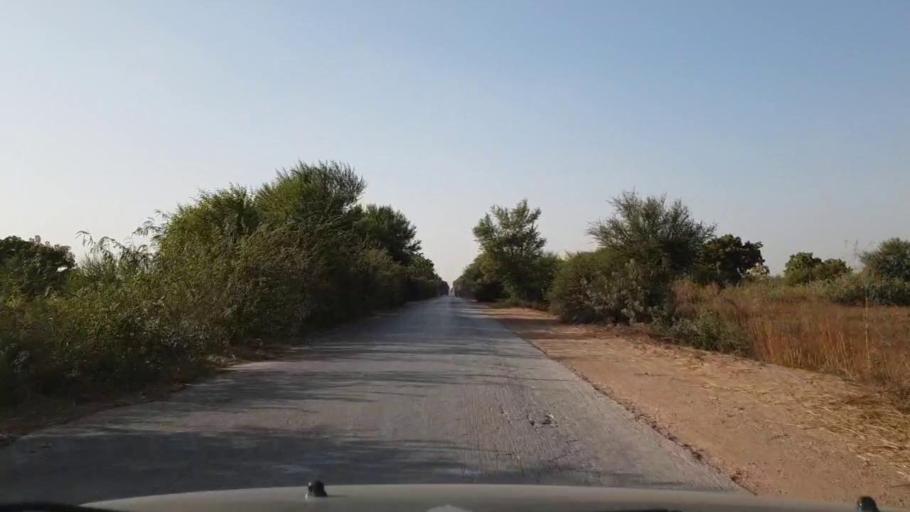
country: PK
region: Sindh
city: Tando Ghulam Ali
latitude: 25.1974
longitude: 68.7995
